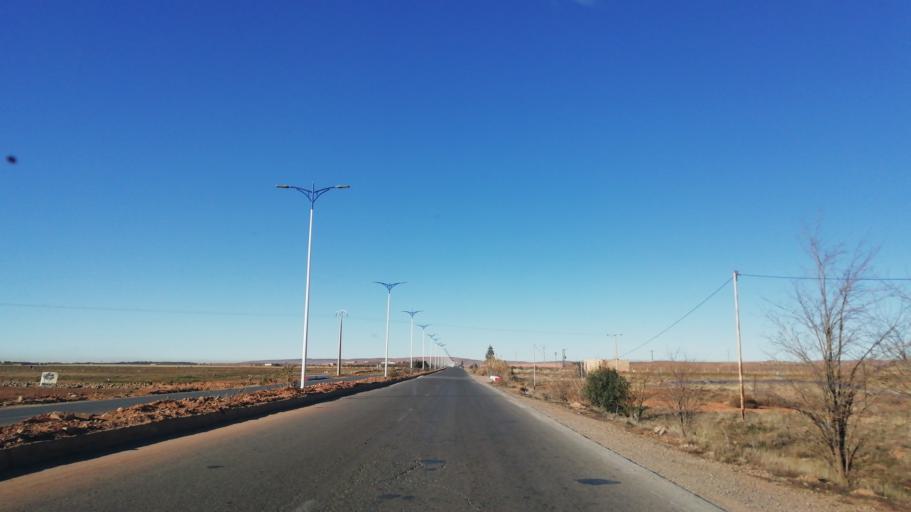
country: DZ
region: El Bayadh
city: El Bayadh
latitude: 33.6906
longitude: 1.0709
